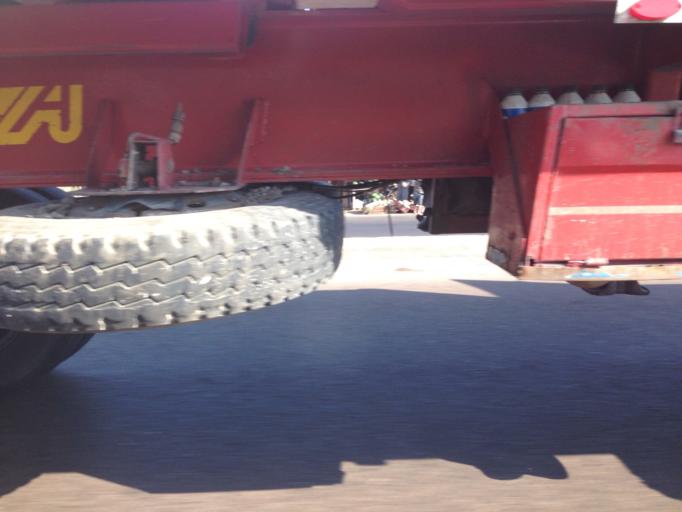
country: EG
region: Al Buhayrah
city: Idku
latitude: 31.2789
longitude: 30.2217
